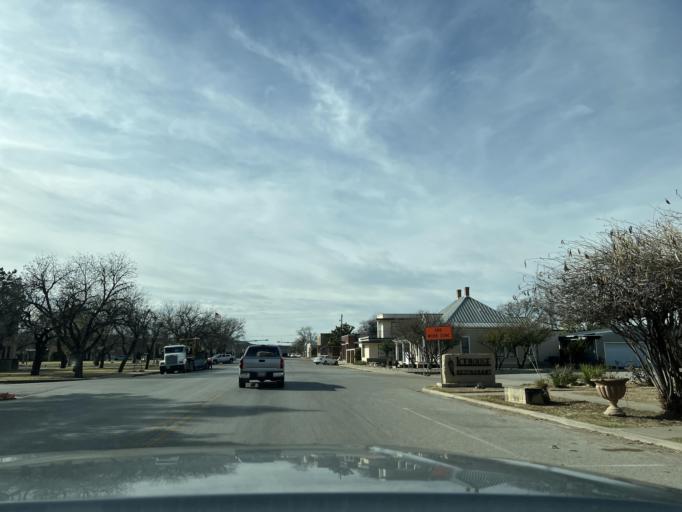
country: US
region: Texas
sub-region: Shackelford County
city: Albany
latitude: 32.7234
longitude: -99.2952
